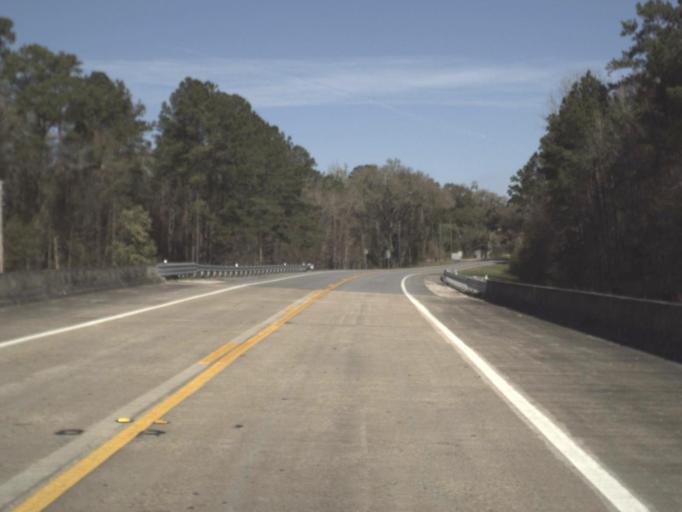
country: US
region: Florida
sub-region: Jefferson County
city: Monticello
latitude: 30.4747
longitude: -84.0220
